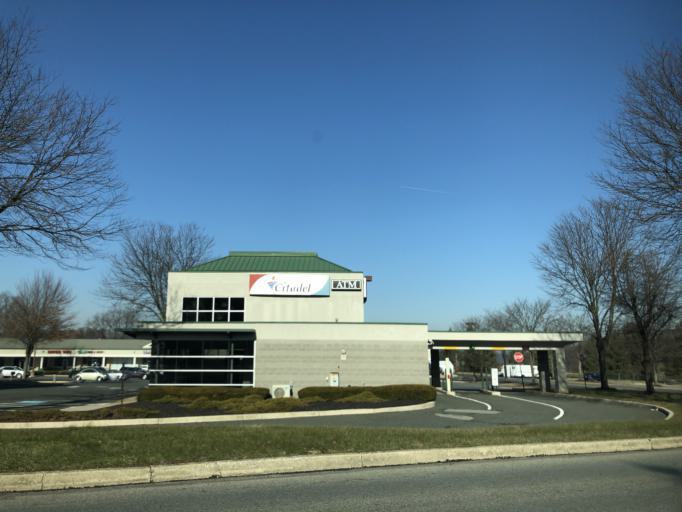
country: US
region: Pennsylvania
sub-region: Chester County
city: Chester Springs
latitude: 40.0661
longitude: -75.6482
